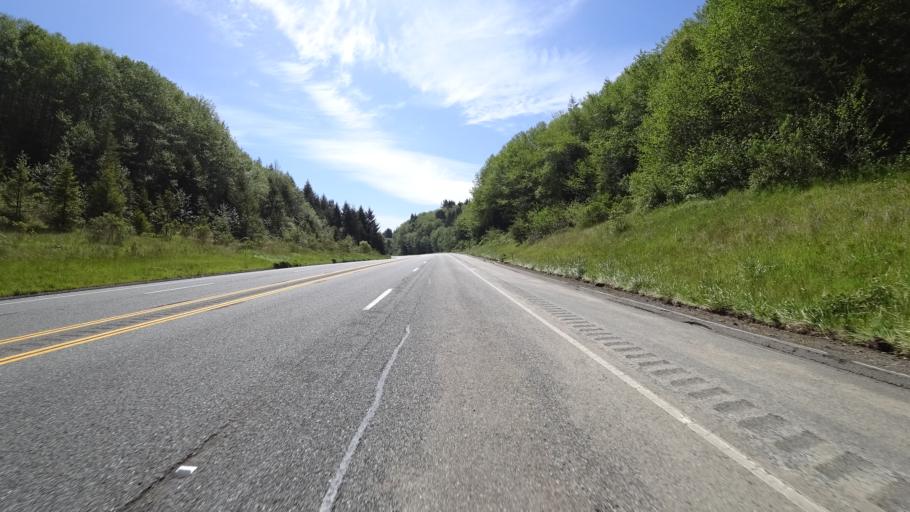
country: US
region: California
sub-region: Del Norte County
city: Bertsch-Oceanview
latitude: 41.4619
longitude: -124.0352
